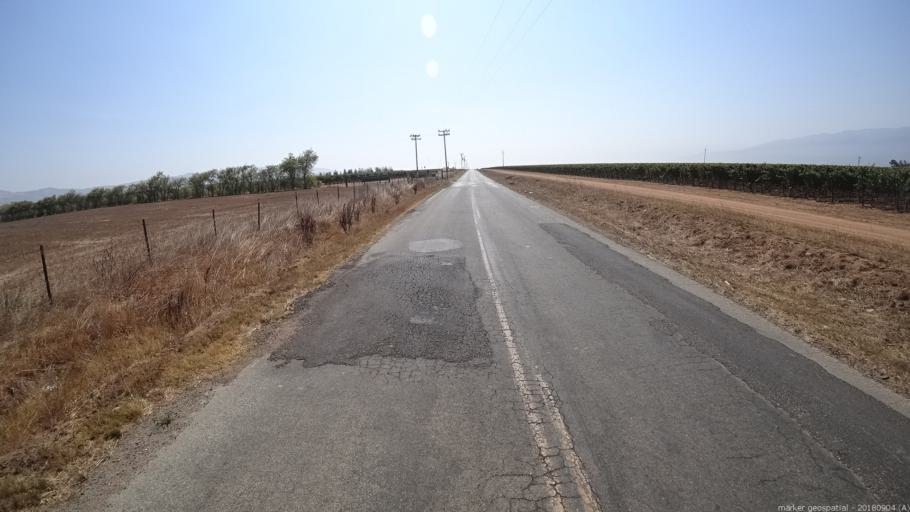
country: US
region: California
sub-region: Monterey County
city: Gonzales
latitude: 36.5133
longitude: -121.4093
